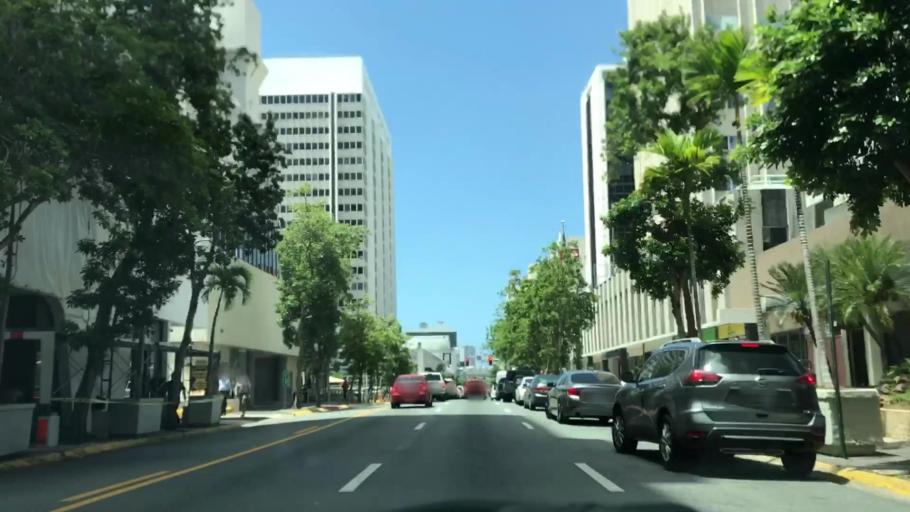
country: PR
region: Catano
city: Catano
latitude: 18.4249
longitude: -66.0576
